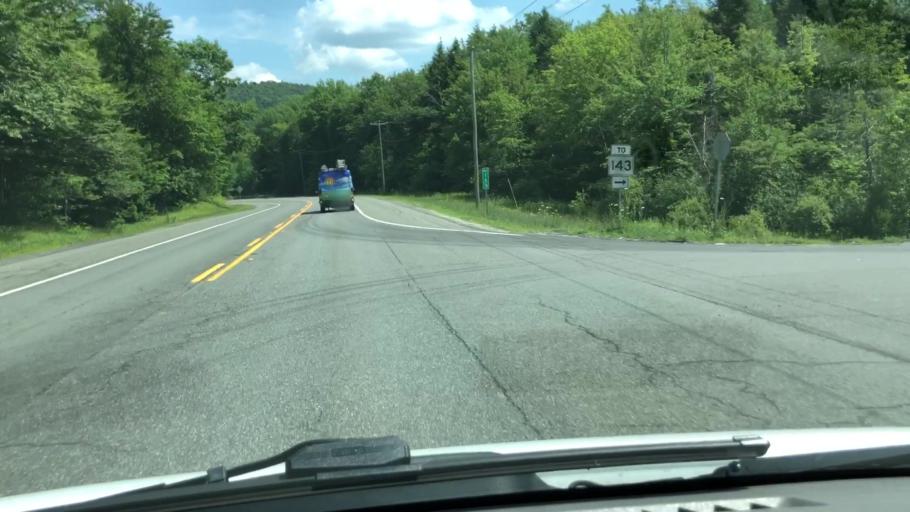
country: US
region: Massachusetts
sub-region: Berkshire County
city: Hinsdale
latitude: 42.4839
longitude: -72.9870
